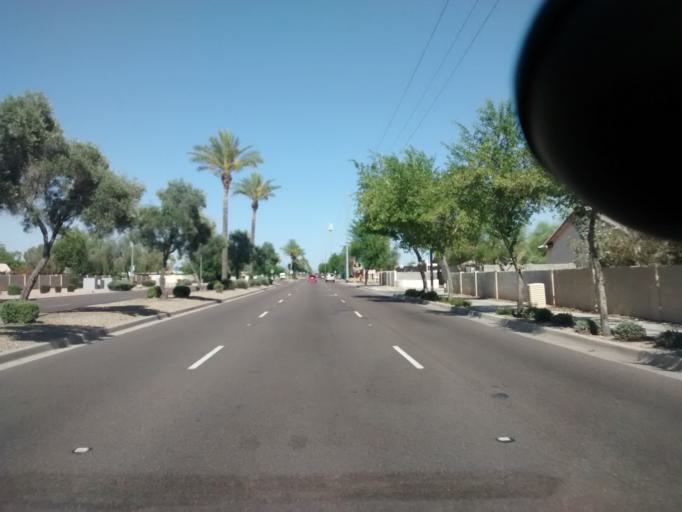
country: US
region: Arizona
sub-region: Maricopa County
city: Peoria
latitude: 33.5378
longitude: -112.2352
